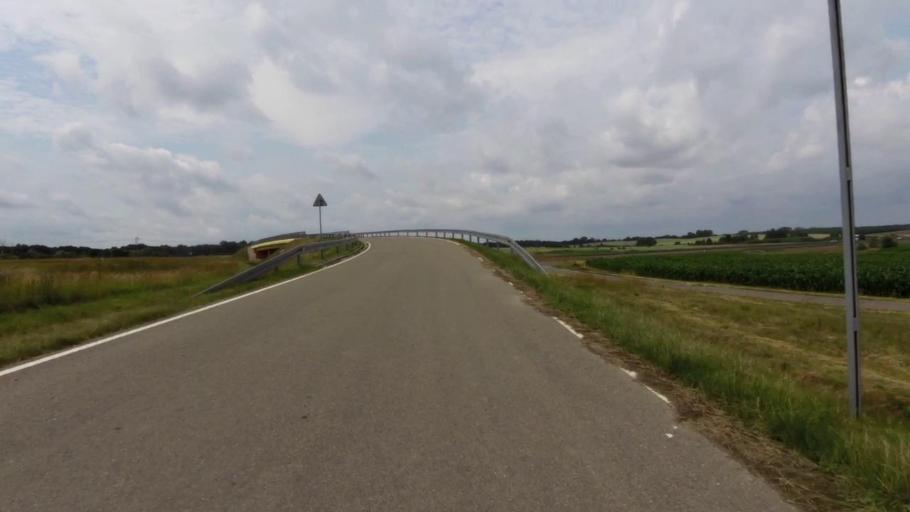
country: PL
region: West Pomeranian Voivodeship
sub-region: Powiat mysliborski
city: Mysliborz
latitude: 52.9793
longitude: 14.9000
